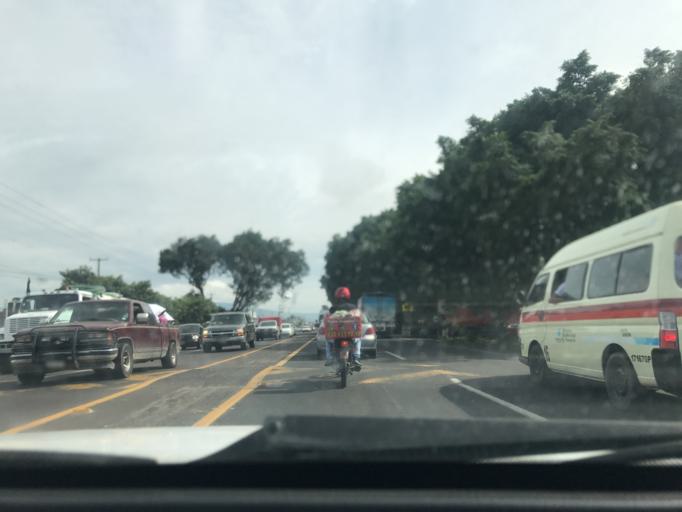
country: MX
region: Morelos
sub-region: Atlatlahucan
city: Colonia San Francisco
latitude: 18.8820
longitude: -98.9189
